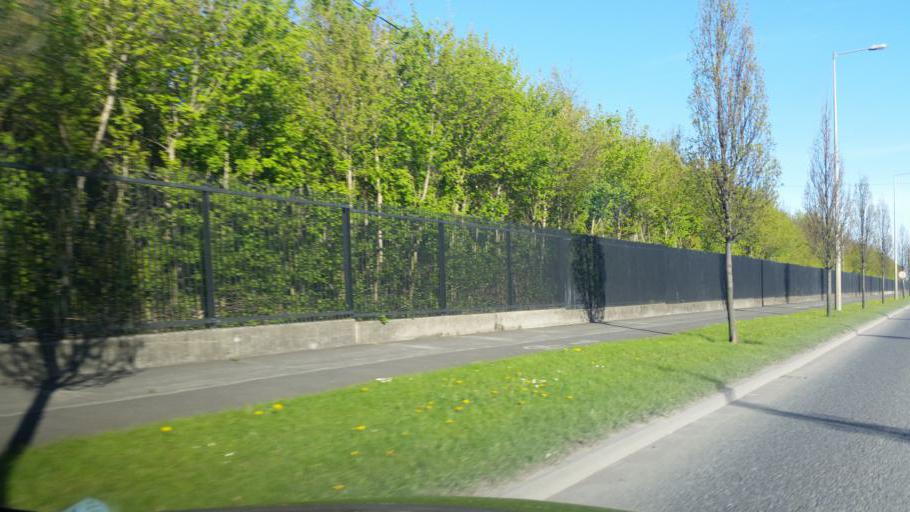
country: IE
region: Leinster
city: Castleknock
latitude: 53.4026
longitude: -6.3377
